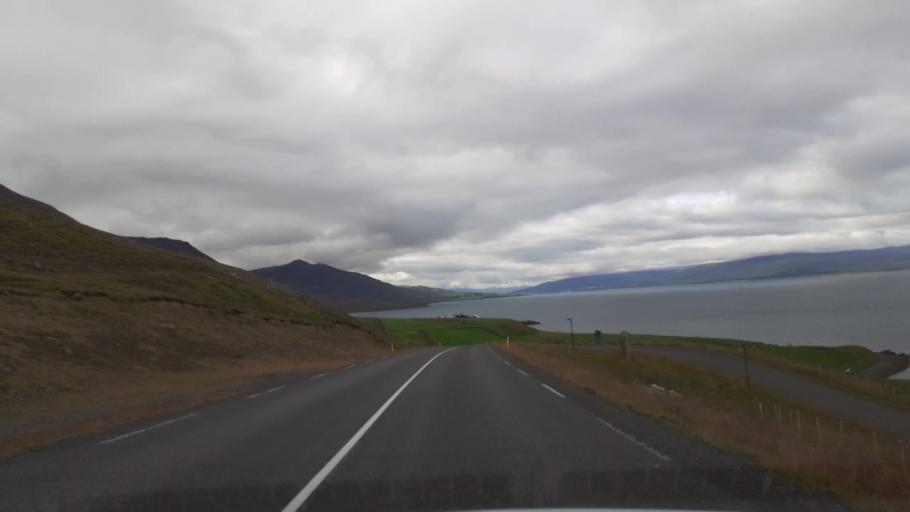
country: IS
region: Northeast
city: Akureyri
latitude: 65.8702
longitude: -18.0761
